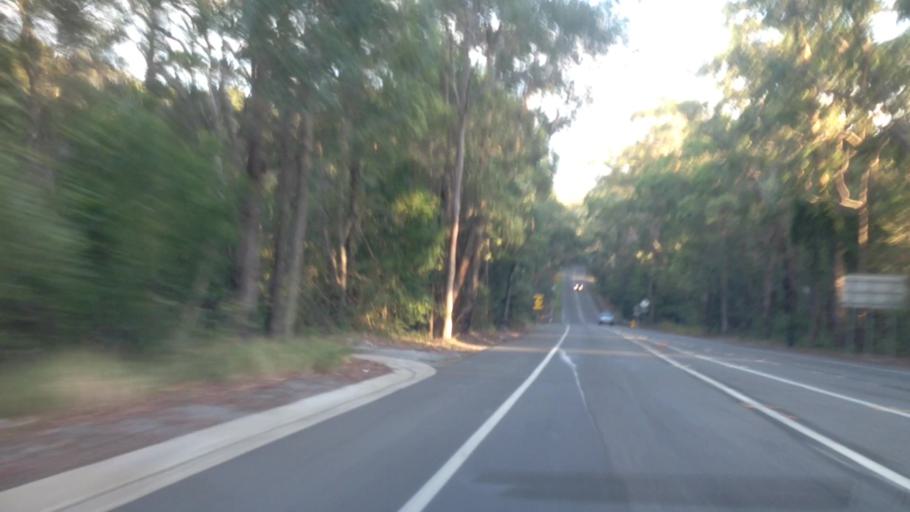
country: AU
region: New South Wales
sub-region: Lake Macquarie Shire
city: Cooranbong
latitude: -32.9751
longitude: 151.4822
